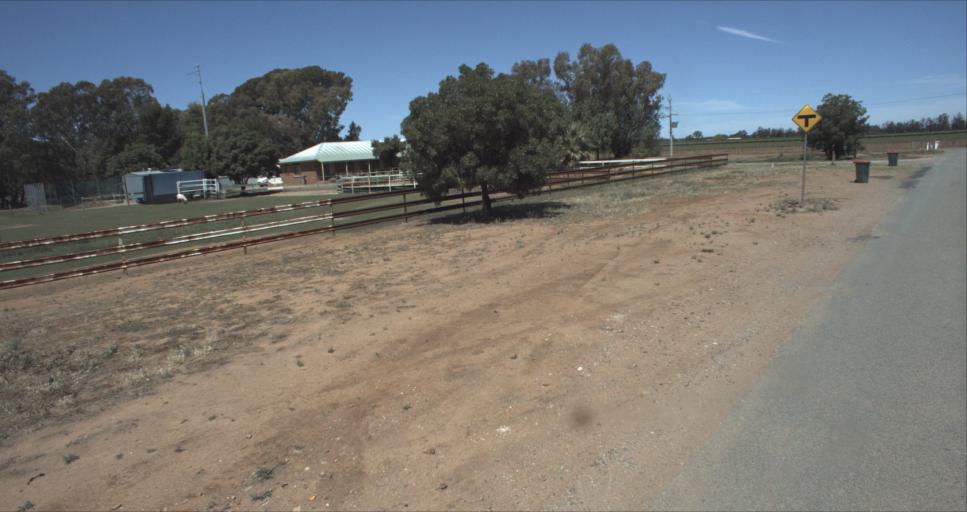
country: AU
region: New South Wales
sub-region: Leeton
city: Leeton
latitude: -34.5302
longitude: 146.3333
